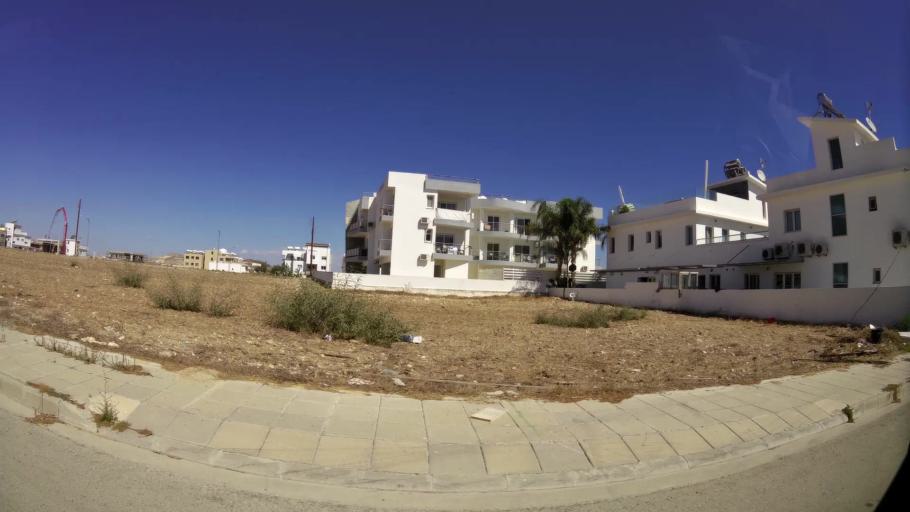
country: CY
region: Larnaka
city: Livadia
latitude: 34.9534
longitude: 33.6372
